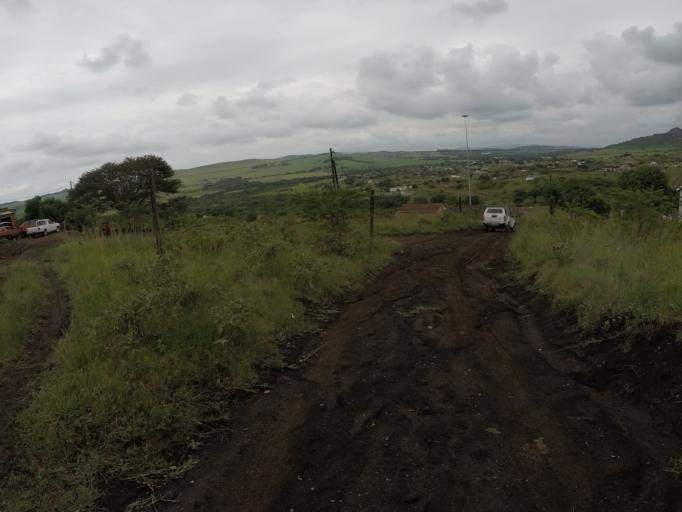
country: ZA
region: KwaZulu-Natal
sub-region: uThungulu District Municipality
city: Empangeni
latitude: -28.7086
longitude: 31.8506
